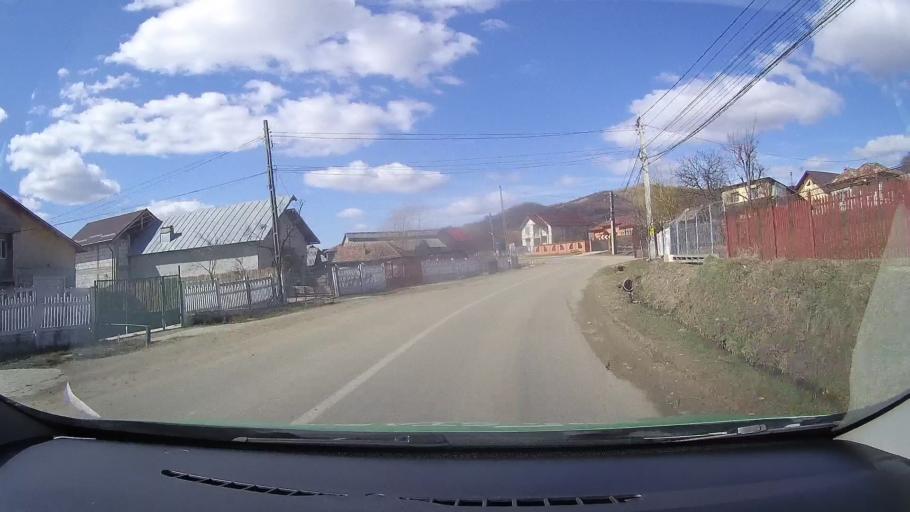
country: RO
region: Dambovita
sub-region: Comuna Glodeni
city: Glodeni
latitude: 45.0207
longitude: 25.4509
